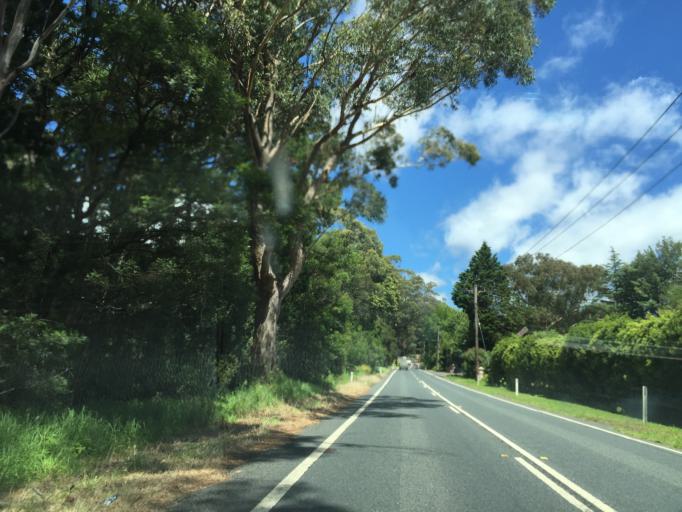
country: AU
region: New South Wales
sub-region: Blue Mountains Municipality
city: Lawson
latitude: -33.5162
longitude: 150.4712
